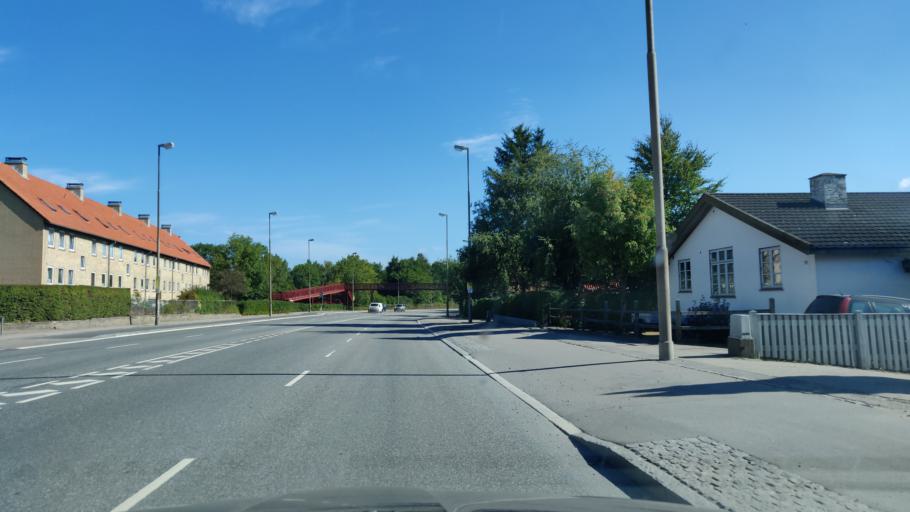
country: DK
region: Zealand
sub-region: Roskilde Kommune
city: Roskilde
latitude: 55.6363
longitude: 12.1092
